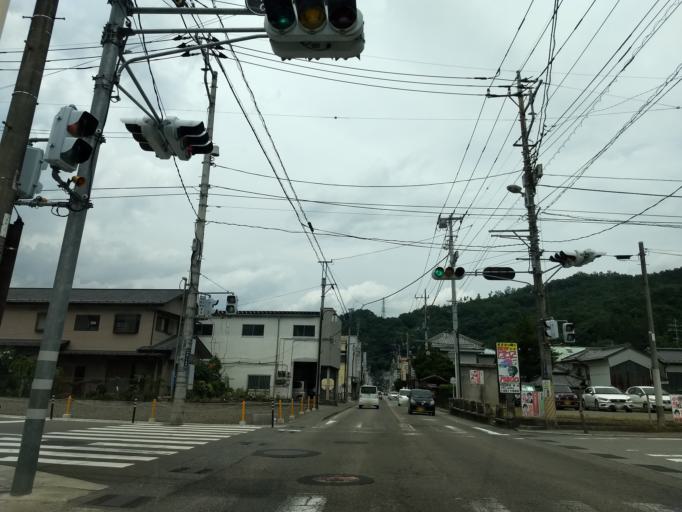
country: JP
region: Yamanashi
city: Otsuki
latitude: 35.5515
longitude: 138.9081
